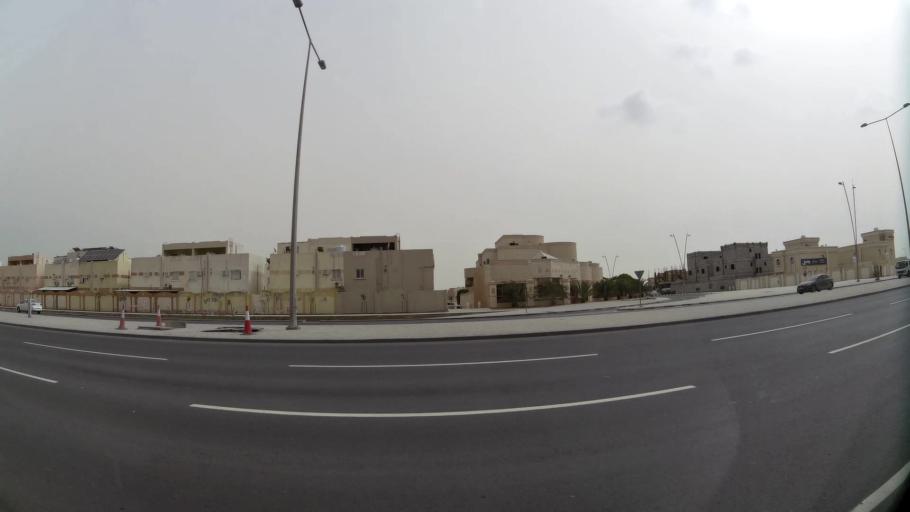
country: QA
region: Baladiyat ad Dawhah
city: Doha
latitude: 25.2387
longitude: 51.5407
